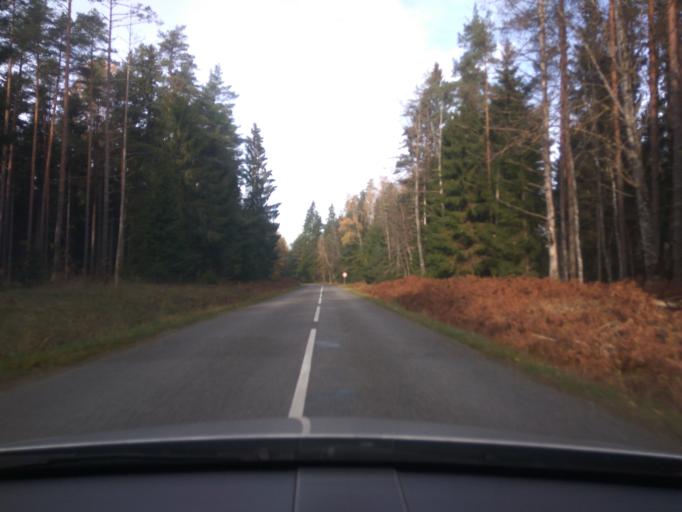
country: LV
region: Alsunga
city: Alsunga
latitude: 56.9977
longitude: 21.4886
